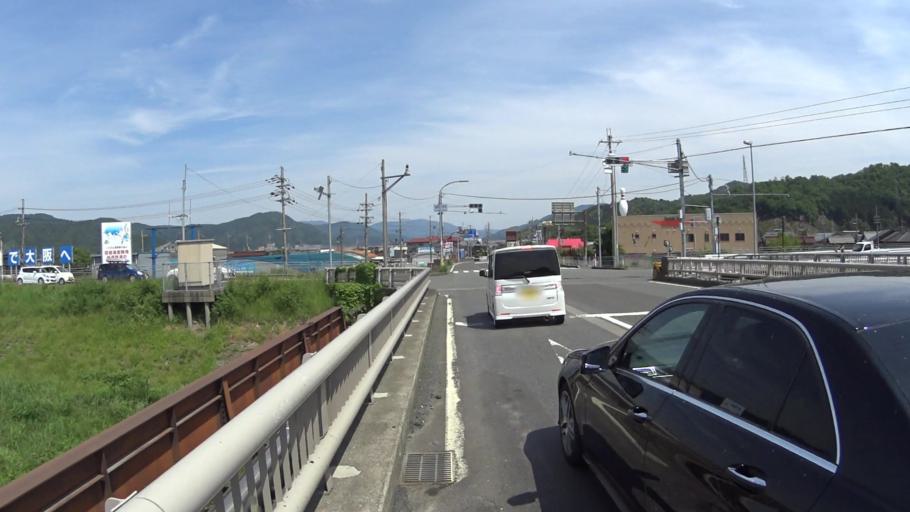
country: JP
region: Fukui
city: Obama
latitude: 35.4888
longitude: 135.7579
